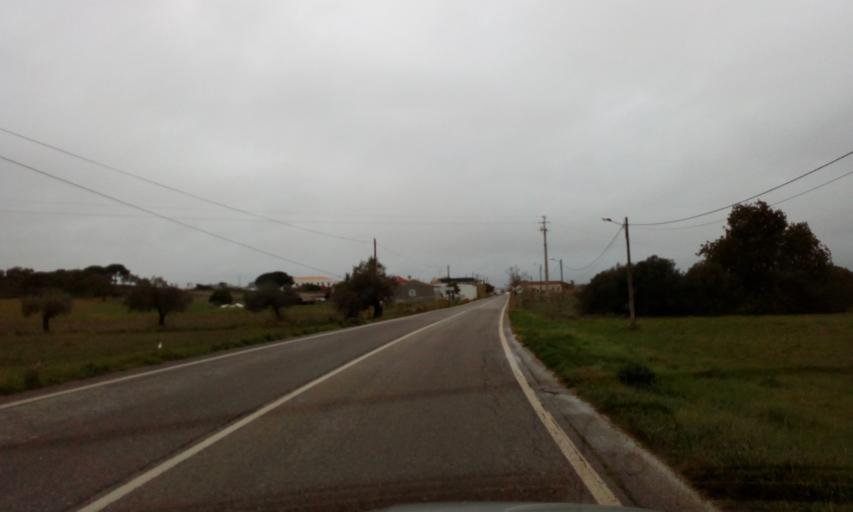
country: PT
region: Faro
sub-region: Albufeira
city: Guia
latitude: 37.1558
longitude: -8.2861
